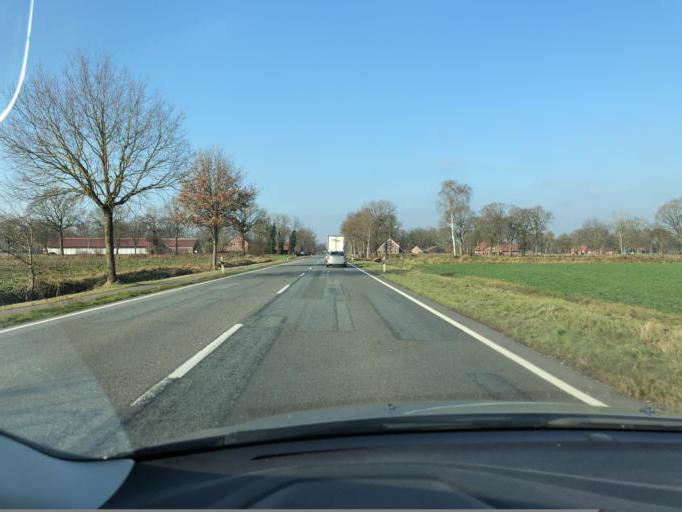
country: DE
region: Lower Saxony
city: Apen
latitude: 53.3013
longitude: 7.7920
